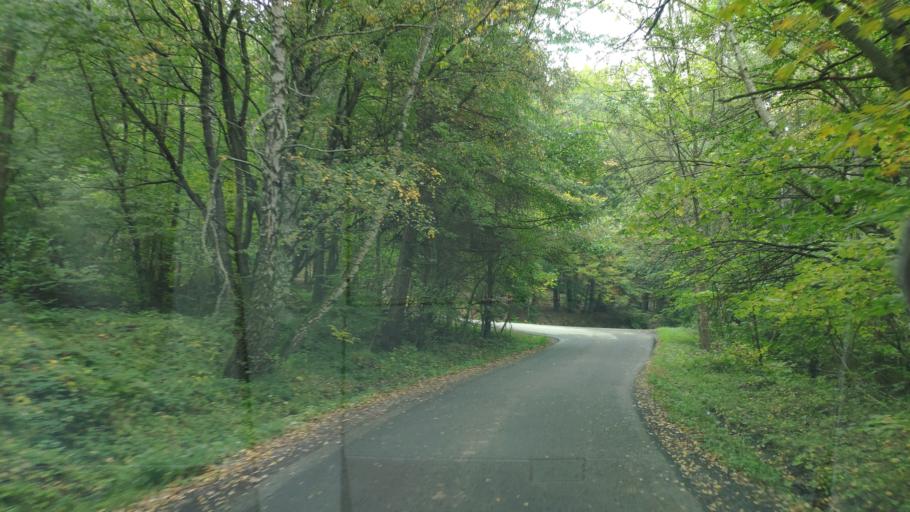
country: SK
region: Presovsky
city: Giraltovce
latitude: 48.9104
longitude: 21.4608
